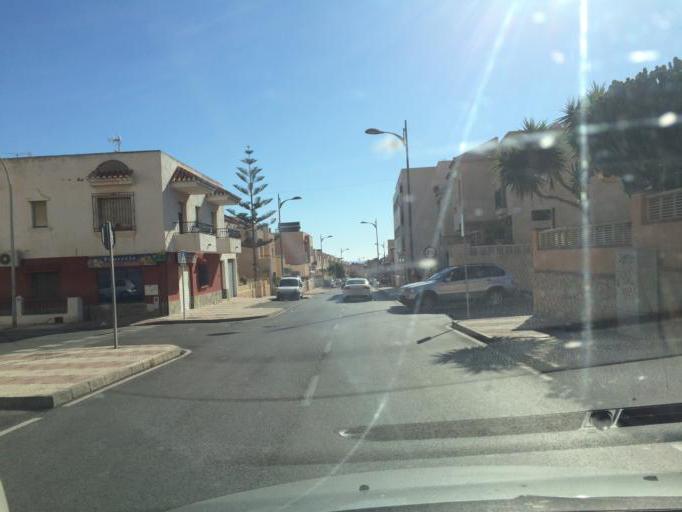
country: ES
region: Andalusia
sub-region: Provincia de Almeria
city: Aguadulce
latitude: 36.8076
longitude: -2.5870
